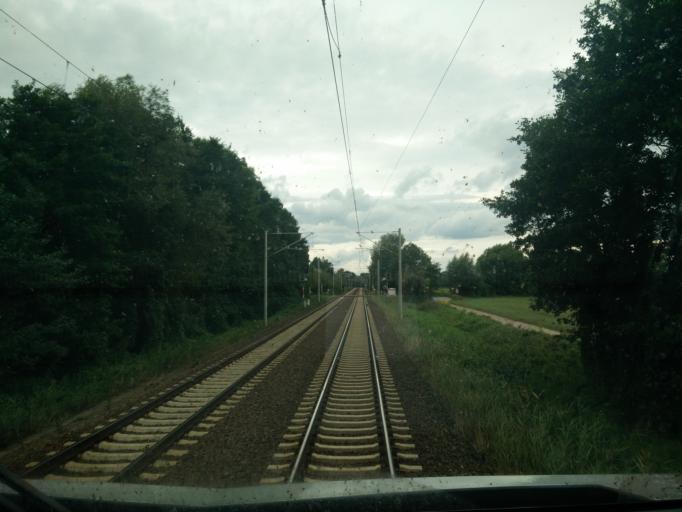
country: DE
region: Brandenburg
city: Lubbenau
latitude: 51.8708
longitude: 13.9348
